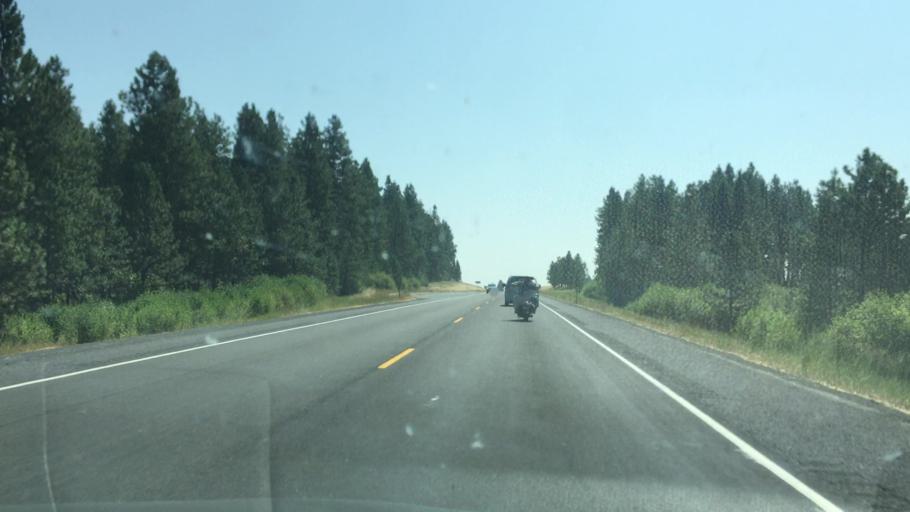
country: US
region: Idaho
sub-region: Nez Perce County
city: Lapwai
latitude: 46.2473
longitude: -116.5950
